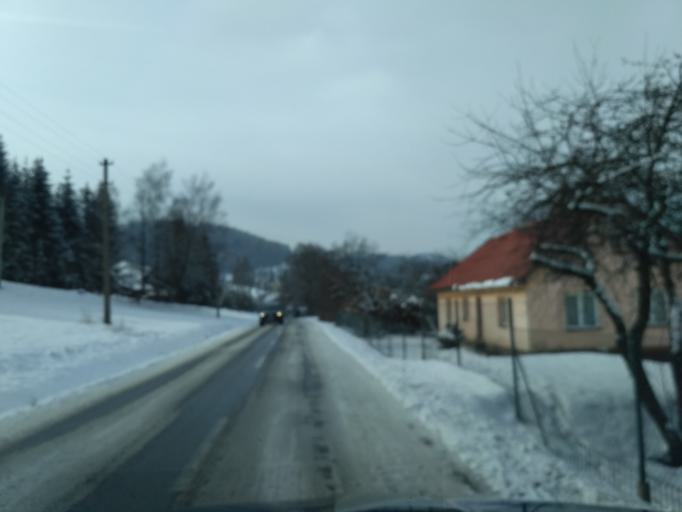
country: CZ
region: Zlin
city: Vidce
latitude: 49.4223
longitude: 18.0810
